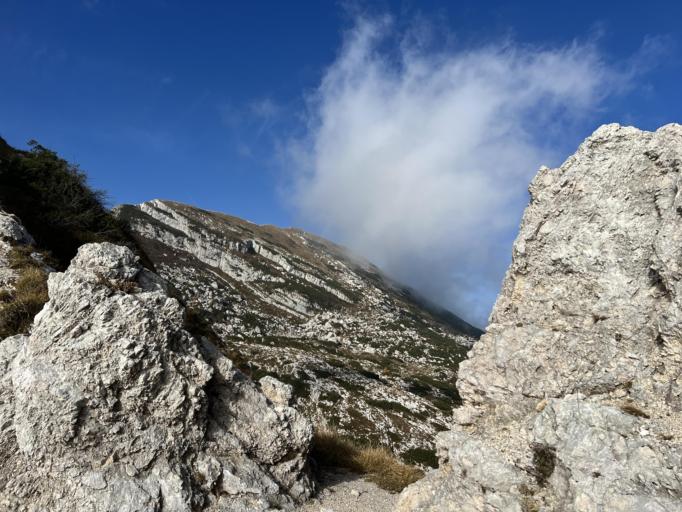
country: IT
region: Friuli Venezia Giulia
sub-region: Provincia di Pordenone
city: Andreis
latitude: 46.2185
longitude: 12.6607
